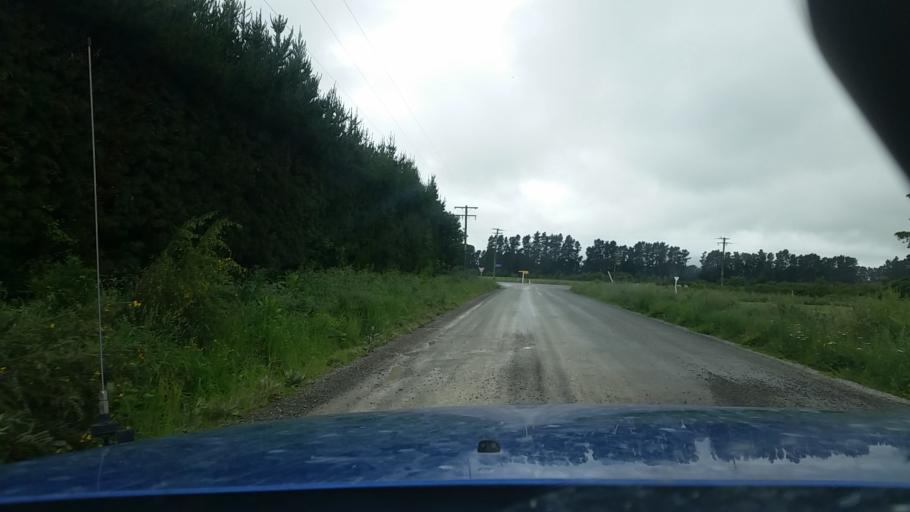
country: NZ
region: Canterbury
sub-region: Ashburton District
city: Methven
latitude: -43.6143
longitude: 171.4905
